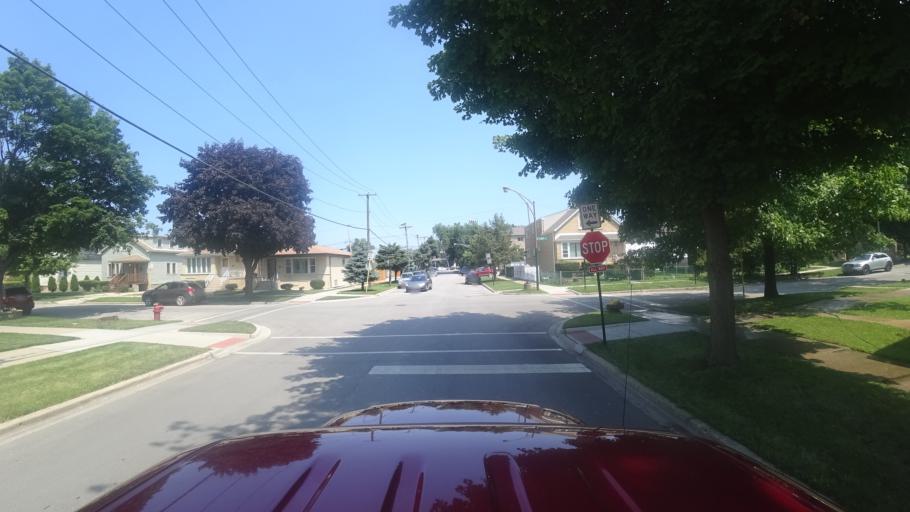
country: US
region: Illinois
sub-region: Cook County
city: Cicero
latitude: 41.7993
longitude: -87.7295
